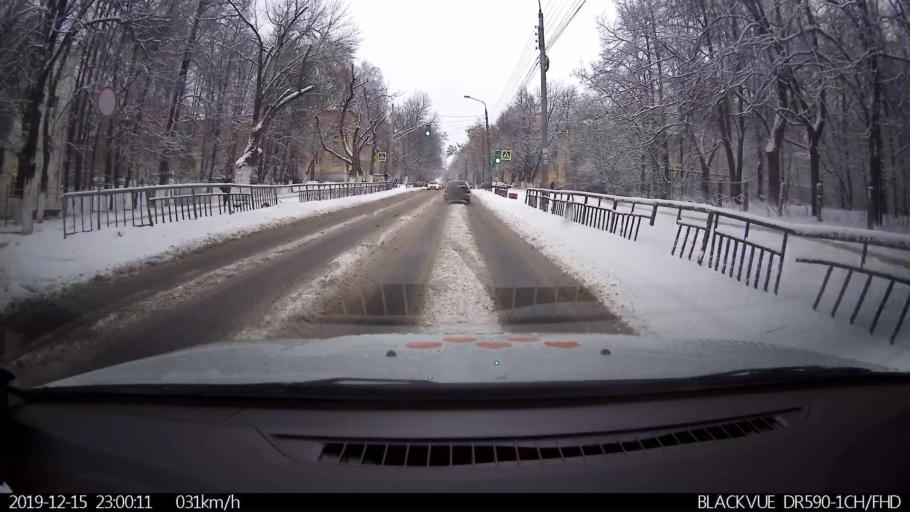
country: RU
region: Nizjnij Novgorod
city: Nizhniy Novgorod
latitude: 56.2608
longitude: 43.9799
